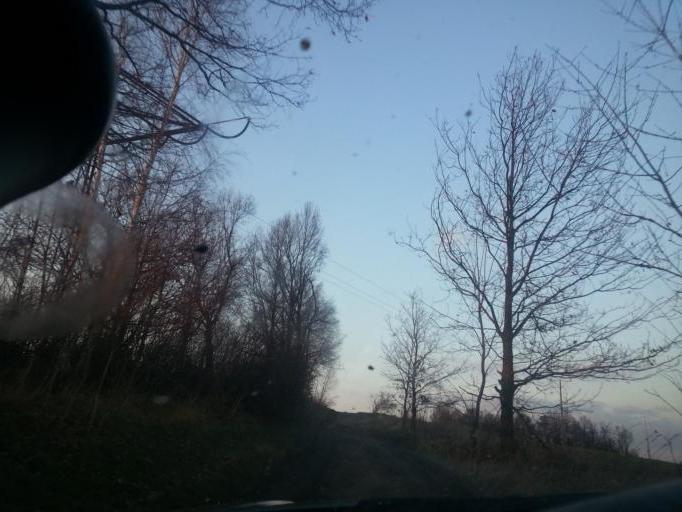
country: PL
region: Lower Silesian Voivodeship
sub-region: Powiat jeleniogorski
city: Stara Kamienica
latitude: 50.9550
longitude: 15.6234
